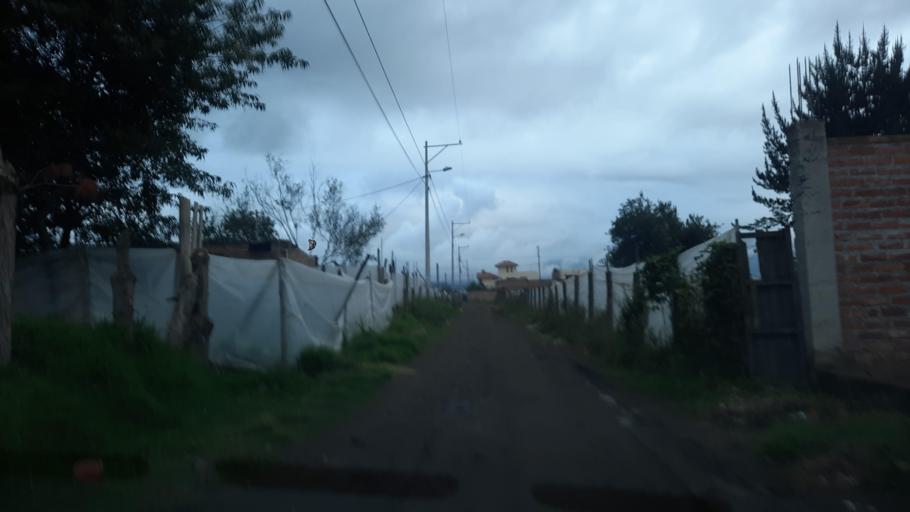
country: EC
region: Chimborazo
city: Riobamba
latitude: -1.6868
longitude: -78.6616
